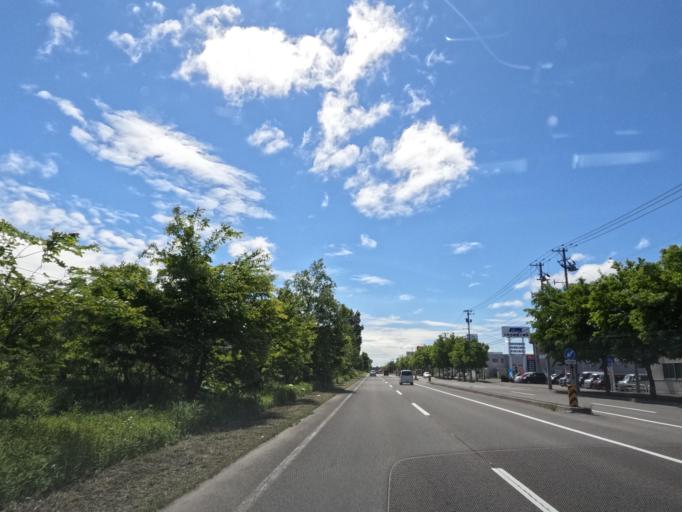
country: JP
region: Hokkaido
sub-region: Asahikawa-shi
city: Asahikawa
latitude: 43.7340
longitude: 142.3637
